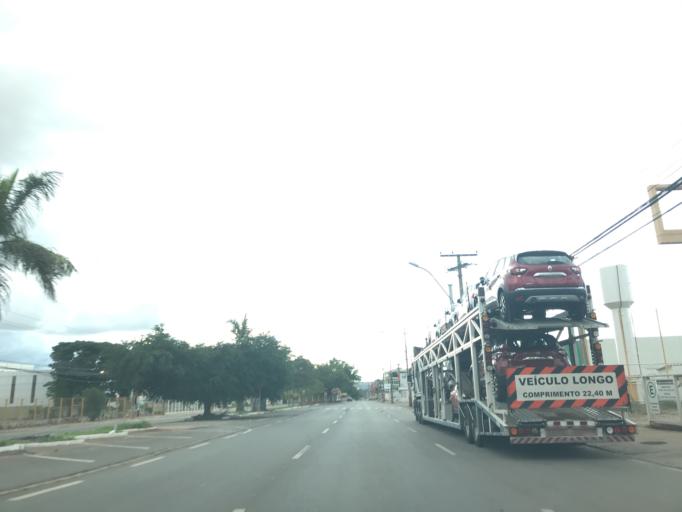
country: BR
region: Federal District
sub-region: Brasilia
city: Brasilia
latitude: -15.8061
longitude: -47.9593
